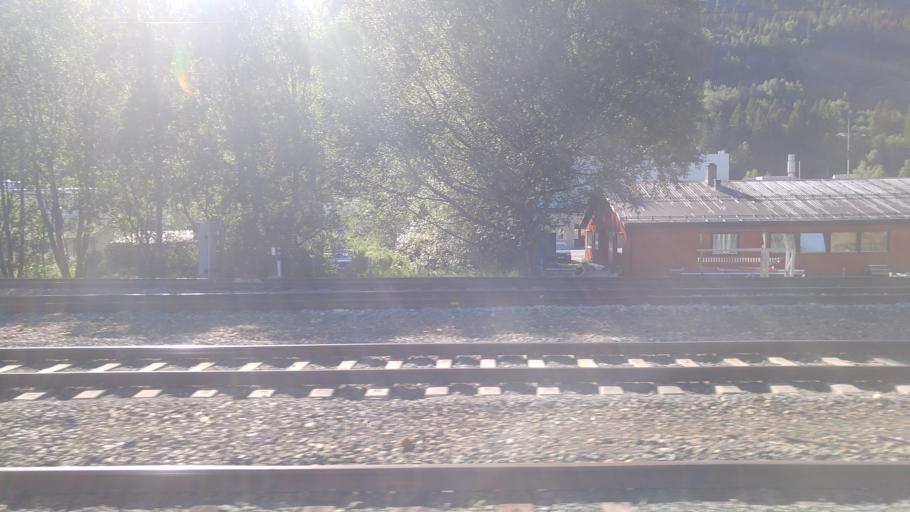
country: NO
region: Sor-Trondelag
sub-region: Midtre Gauldal
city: Storen
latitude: 63.0550
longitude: 10.2872
